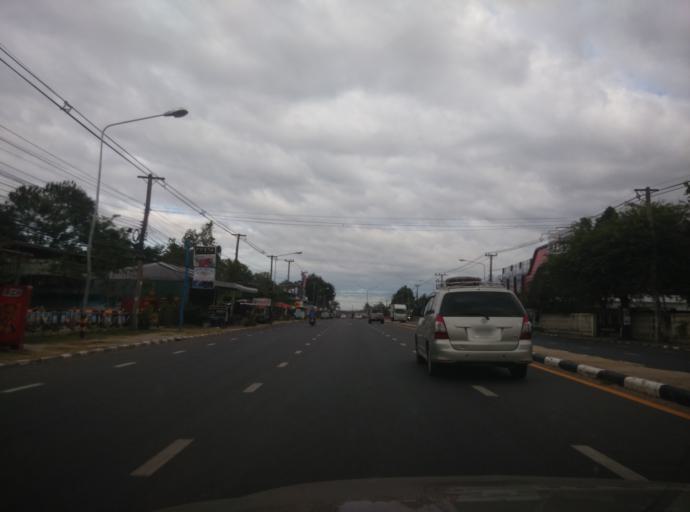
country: TH
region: Sisaket
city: Si Sa Ket
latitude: 15.1108
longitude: 104.3548
